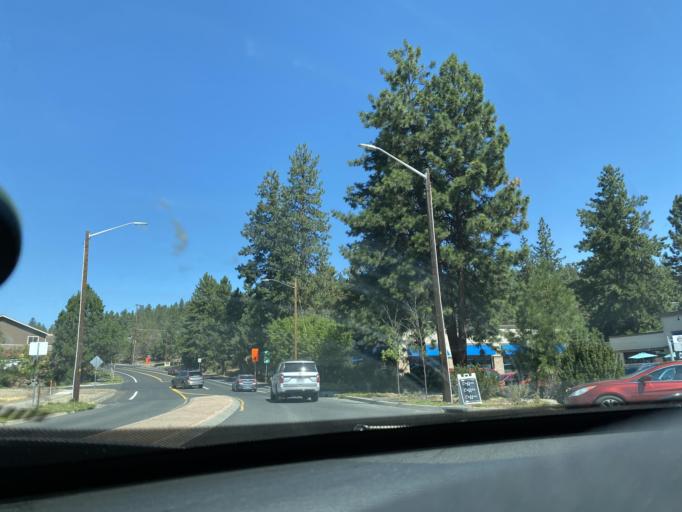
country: US
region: Oregon
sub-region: Deschutes County
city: Bend
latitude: 44.0626
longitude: -121.3380
